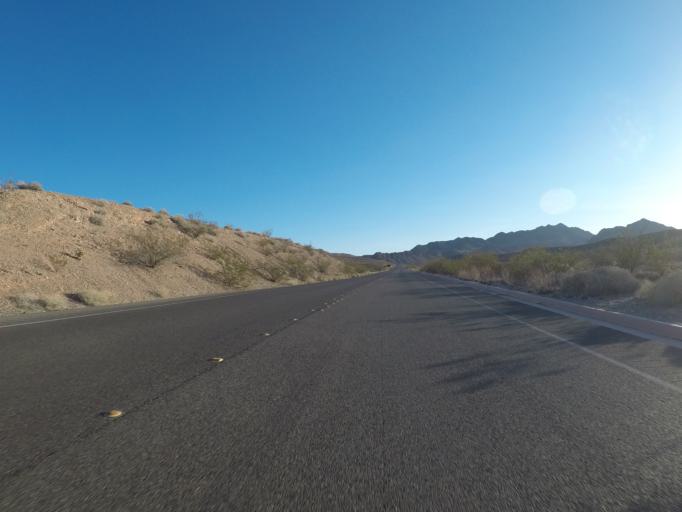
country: US
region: Nevada
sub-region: Clark County
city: Moapa Valley
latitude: 36.2729
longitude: -114.4829
